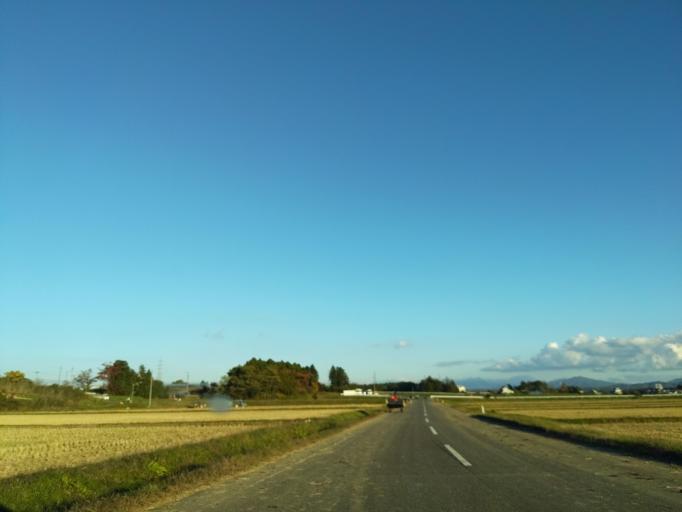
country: JP
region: Fukushima
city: Koriyama
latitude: 37.4529
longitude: 140.3631
